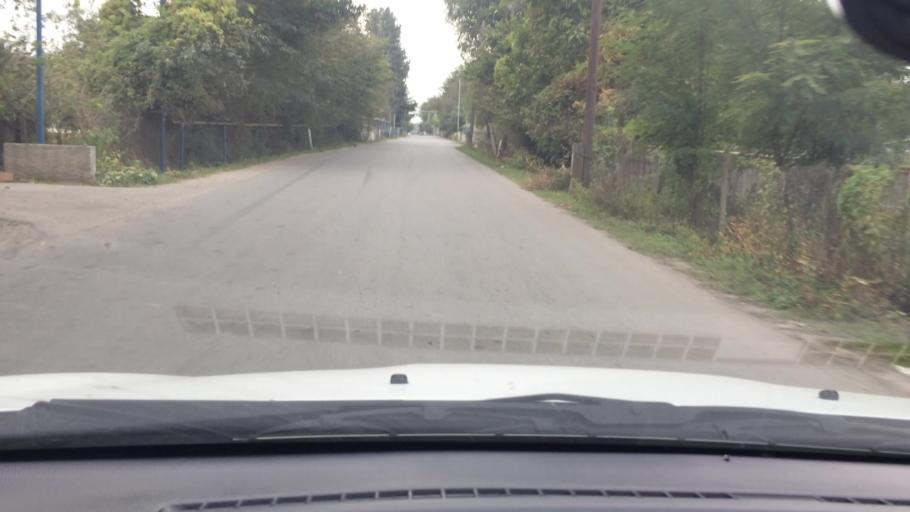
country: AM
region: Tavush
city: Bagratashen
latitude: 41.3329
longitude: 44.9095
